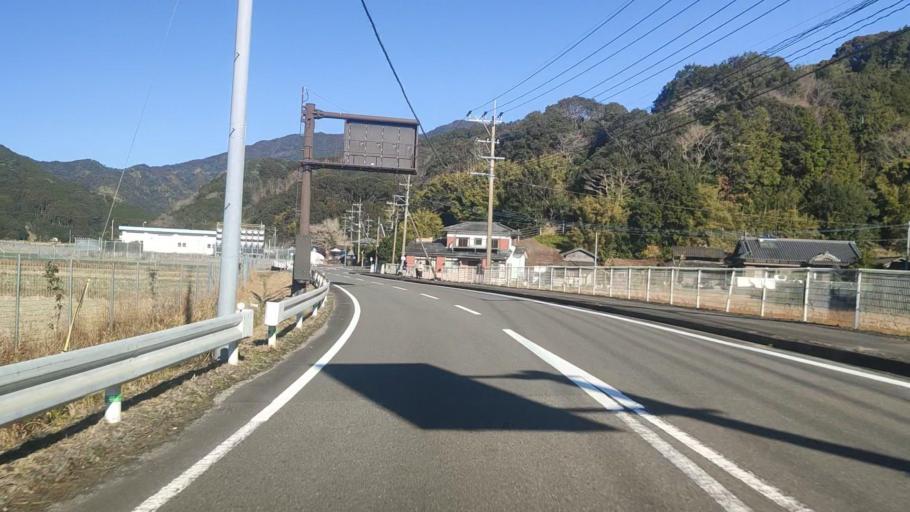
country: JP
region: Miyazaki
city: Nobeoka
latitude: 32.6664
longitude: 131.7667
